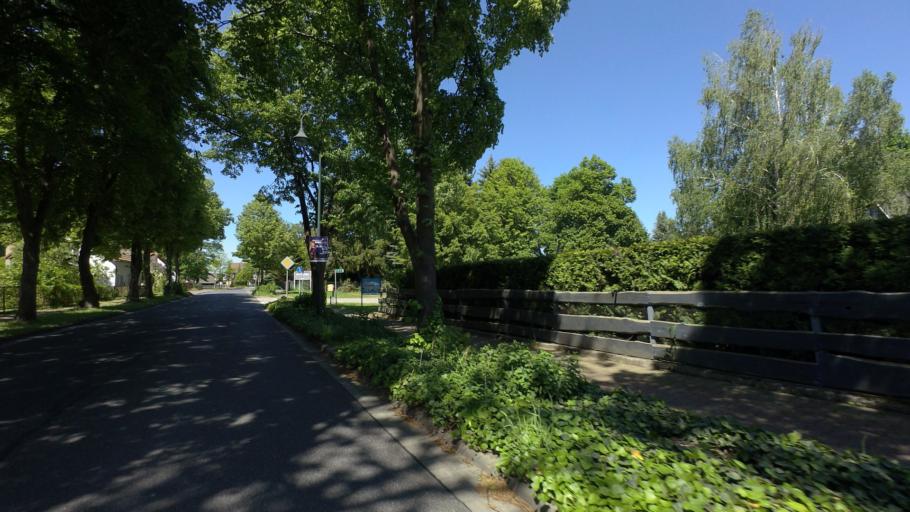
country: DE
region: Brandenburg
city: Lieberose
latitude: 51.9794
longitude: 14.2984
